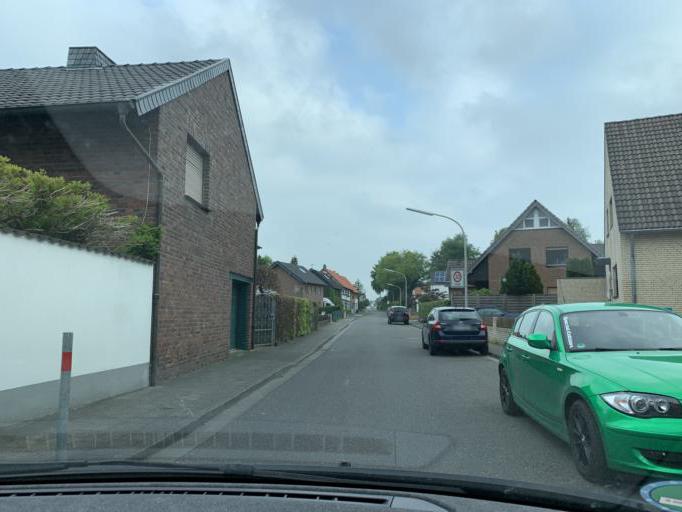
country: DE
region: North Rhine-Westphalia
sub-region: Regierungsbezirk Dusseldorf
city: Monchengladbach
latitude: 51.1138
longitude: 6.4090
